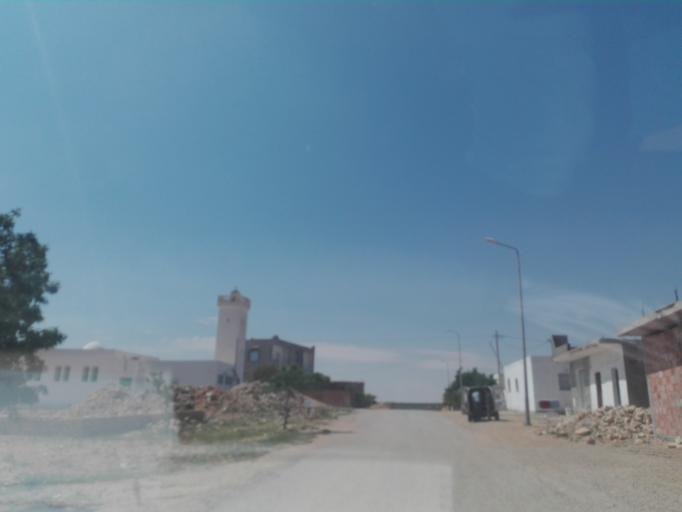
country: TN
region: Safaqis
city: Bi'r `Ali Bin Khalifah
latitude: 34.6124
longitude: 10.3572
